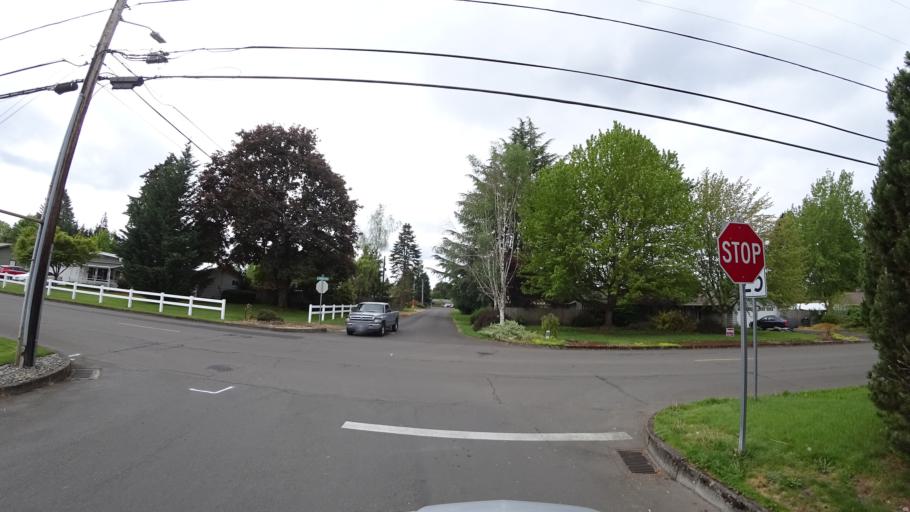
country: US
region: Oregon
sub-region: Washington County
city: Hillsboro
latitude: 45.5328
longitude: -122.9757
